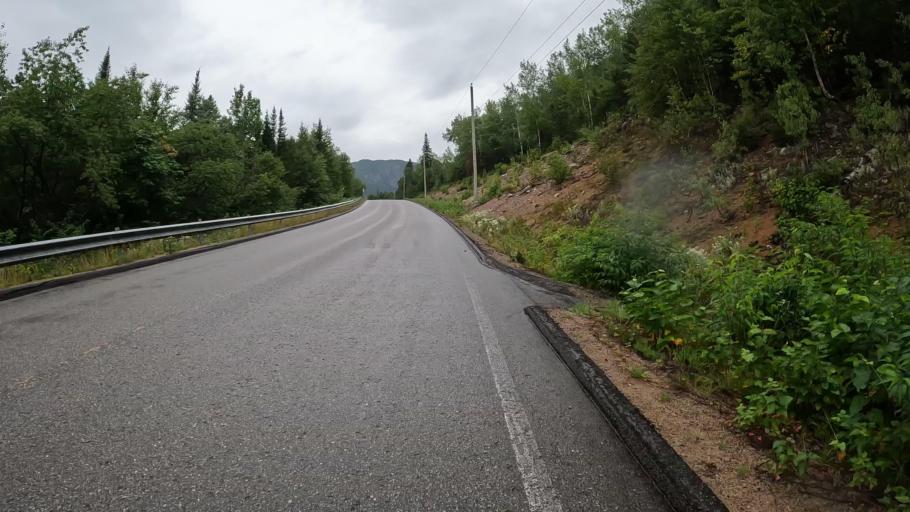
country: CA
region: Quebec
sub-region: Capitale-Nationale
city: La Malbaie
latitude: 47.8595
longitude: -70.4693
